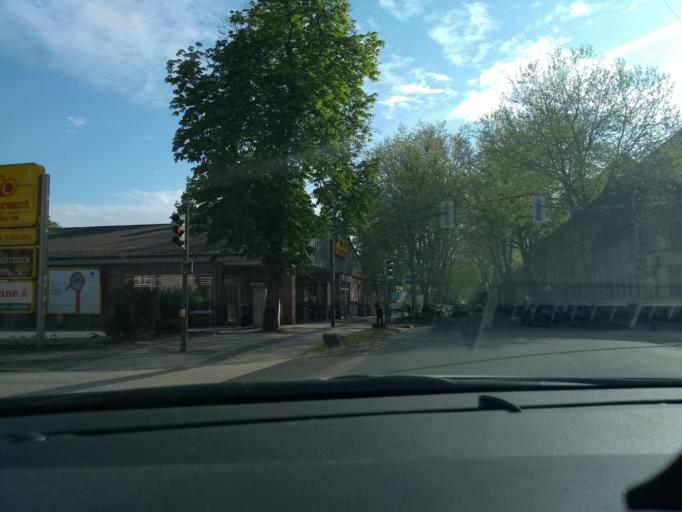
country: DE
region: North Rhine-Westphalia
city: Lunen
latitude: 51.6204
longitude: 7.5359
